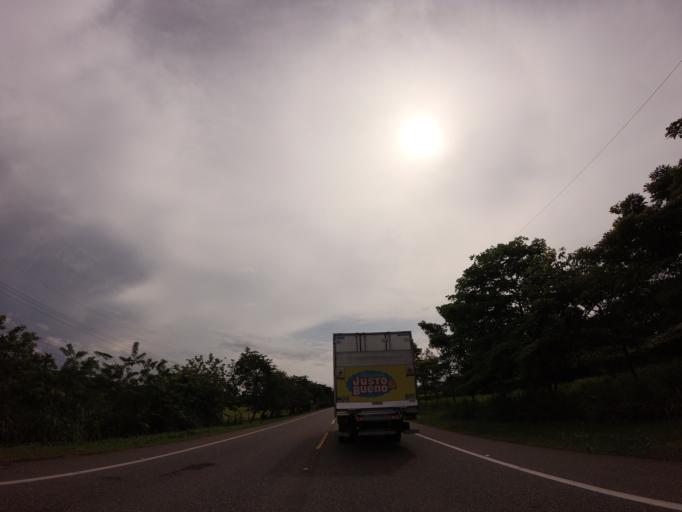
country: CO
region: Caldas
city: La Dorada
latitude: 5.3976
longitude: -74.6988
